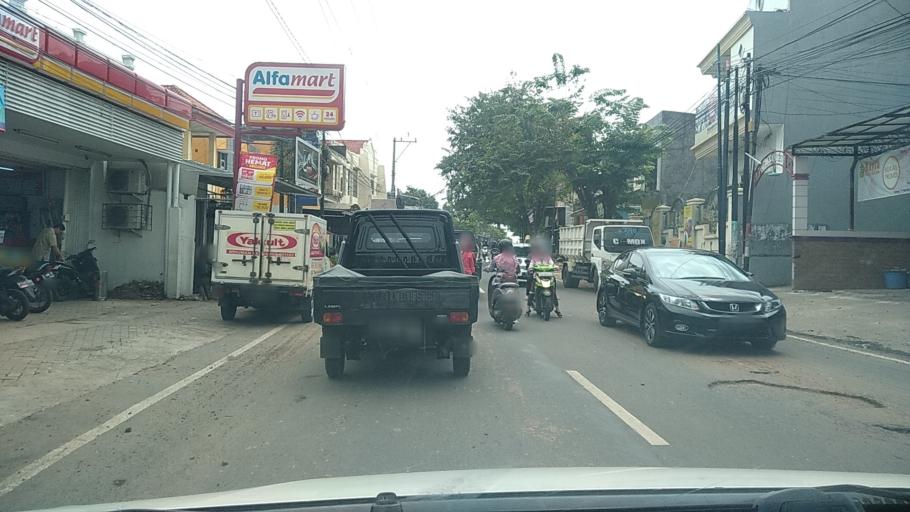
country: ID
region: Central Java
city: Semarang
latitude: -7.0592
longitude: 110.4372
